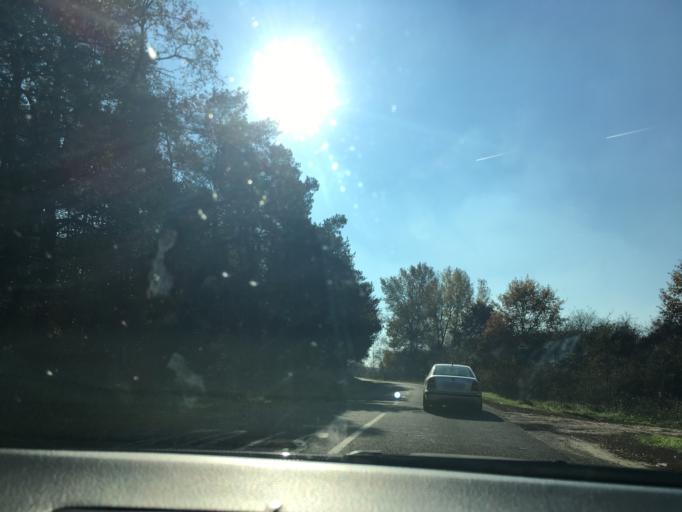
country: HU
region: Hajdu-Bihar
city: Mikepercs
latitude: 47.4844
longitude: 21.7122
